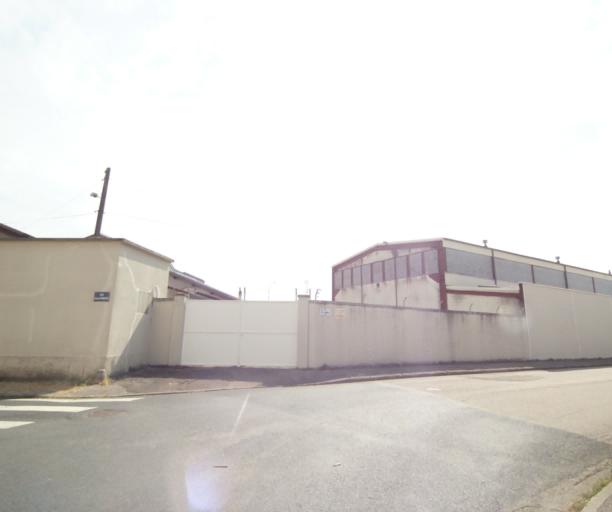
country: FR
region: Lorraine
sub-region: Departement de Meurthe-et-Moselle
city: Luneville
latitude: 48.5901
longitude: 6.5106
